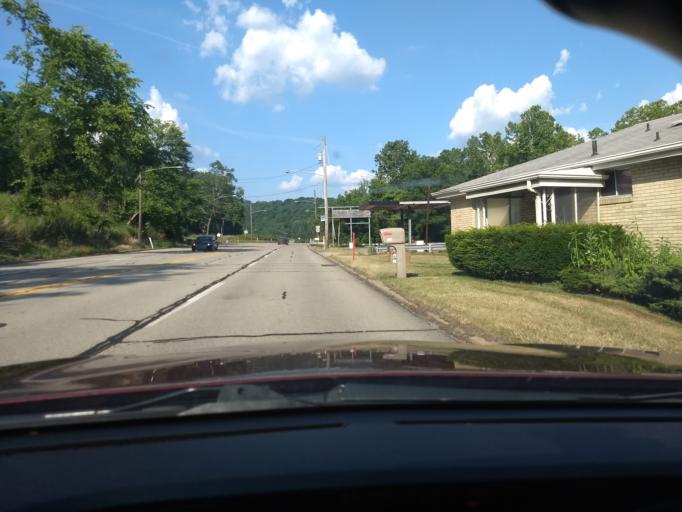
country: US
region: Pennsylvania
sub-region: Allegheny County
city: Versailles
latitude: 40.3218
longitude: -79.8267
